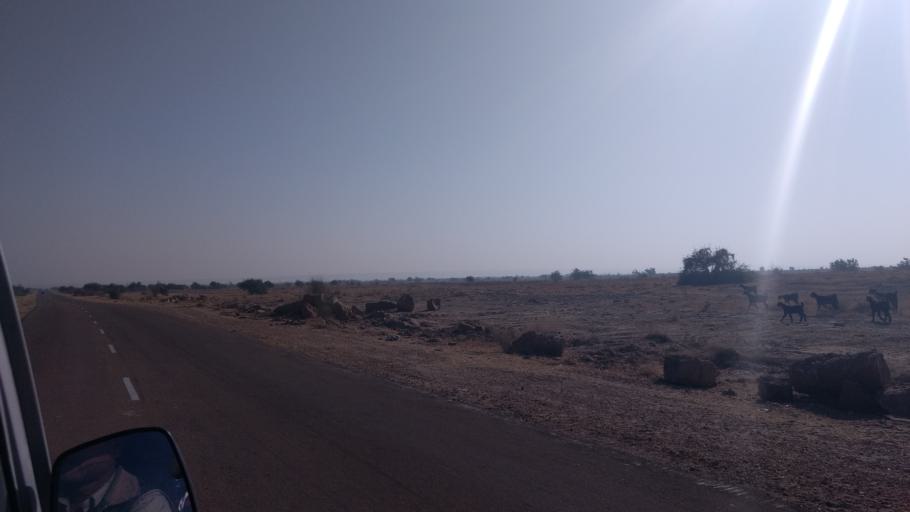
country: IN
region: Rajasthan
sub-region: Jaisalmer
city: Jaisalmer
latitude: 26.9111
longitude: 70.7562
